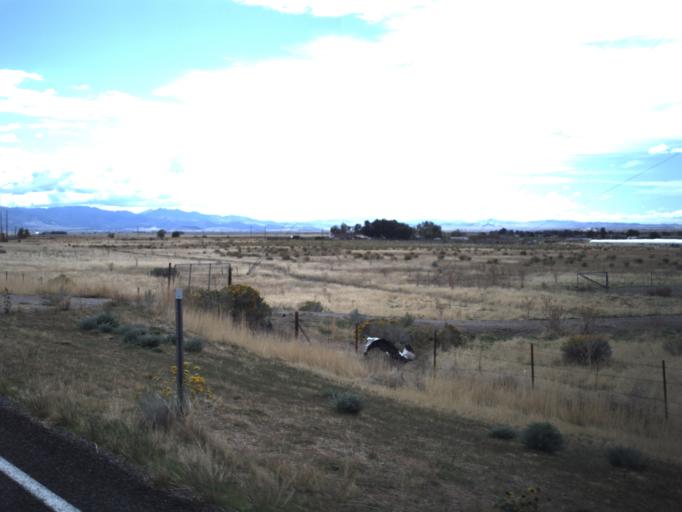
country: US
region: Utah
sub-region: Millard County
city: Fillmore
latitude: 38.9851
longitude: -112.4102
